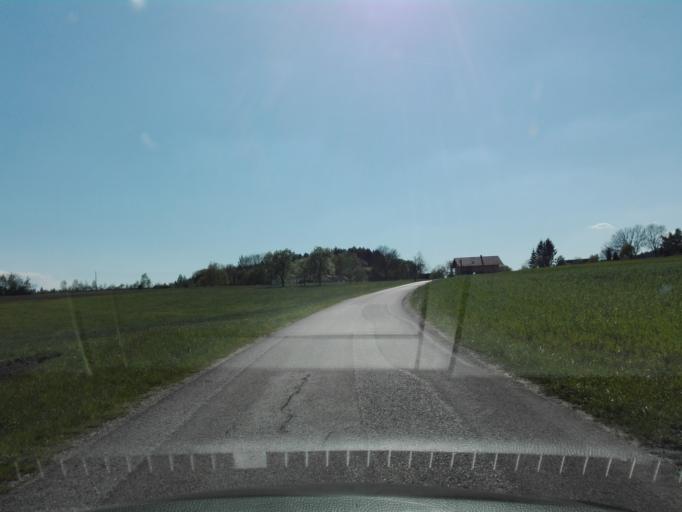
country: DE
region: Bavaria
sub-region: Lower Bavaria
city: Obernzell
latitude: 48.4447
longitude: 13.6890
